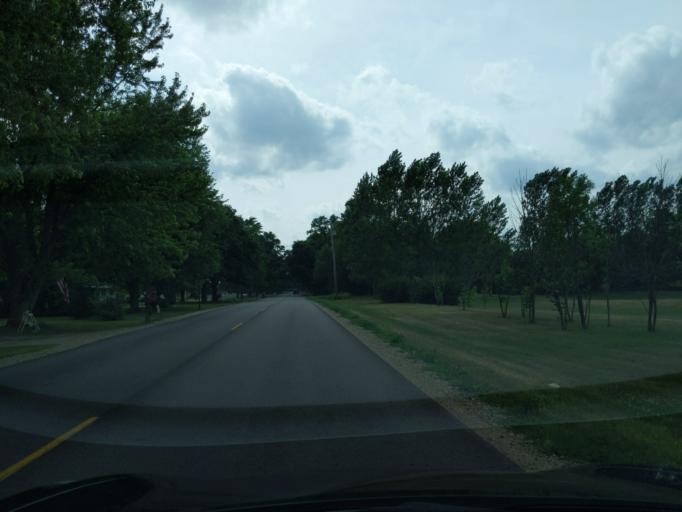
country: US
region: Michigan
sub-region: Eaton County
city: Eaton Rapids
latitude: 42.5093
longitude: -84.6241
